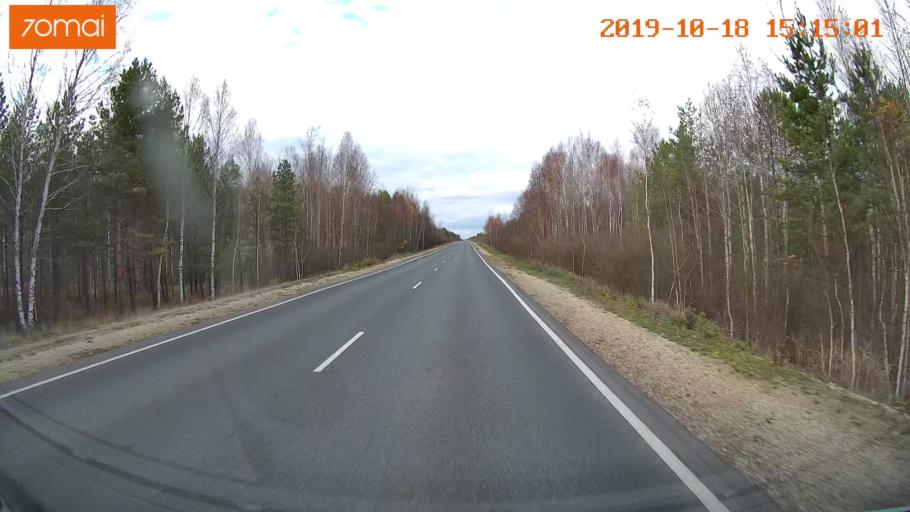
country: RU
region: Vladimir
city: Gus'-Khrustal'nyy
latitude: 55.6121
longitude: 40.7215
